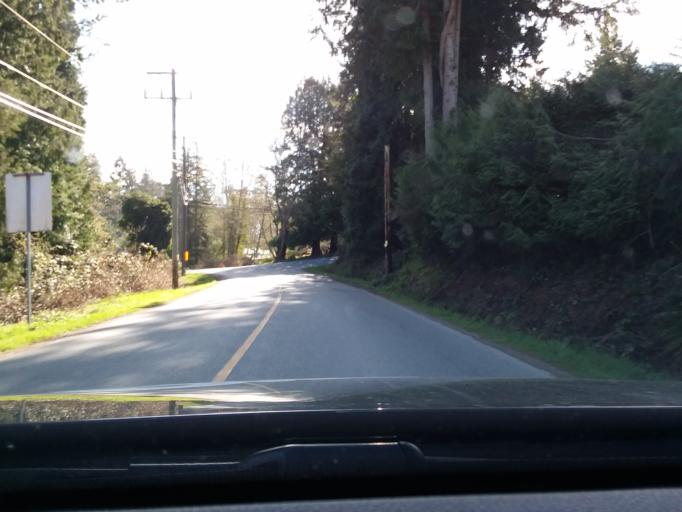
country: CA
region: British Columbia
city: North Saanich
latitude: 48.8793
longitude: -123.3240
